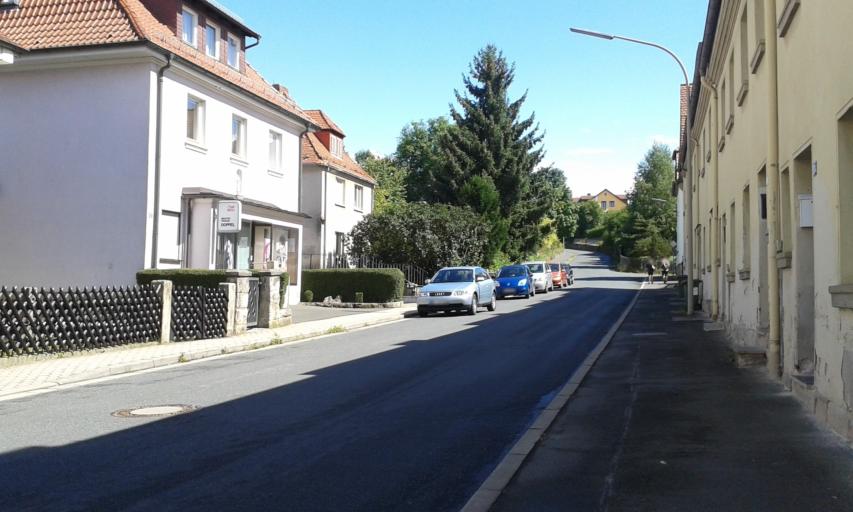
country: DE
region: Bavaria
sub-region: Upper Franconia
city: Kronach
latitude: 50.2385
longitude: 11.3337
